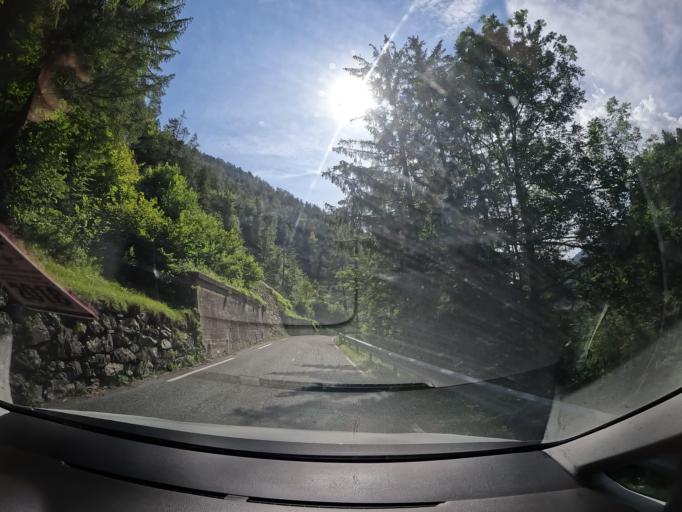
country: AT
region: Carinthia
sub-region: Politischer Bezirk Klagenfurt Land
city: Ludmannsdorf
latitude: 46.5163
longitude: 14.0987
